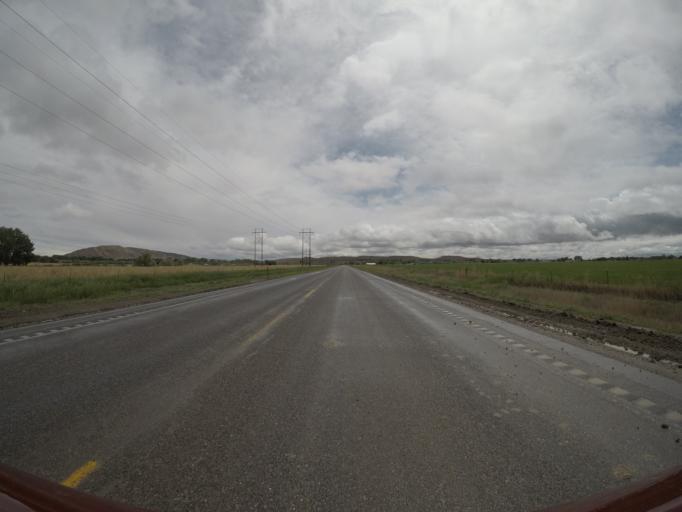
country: US
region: Wyoming
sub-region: Big Horn County
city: Lovell
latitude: 44.8492
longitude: -108.3316
